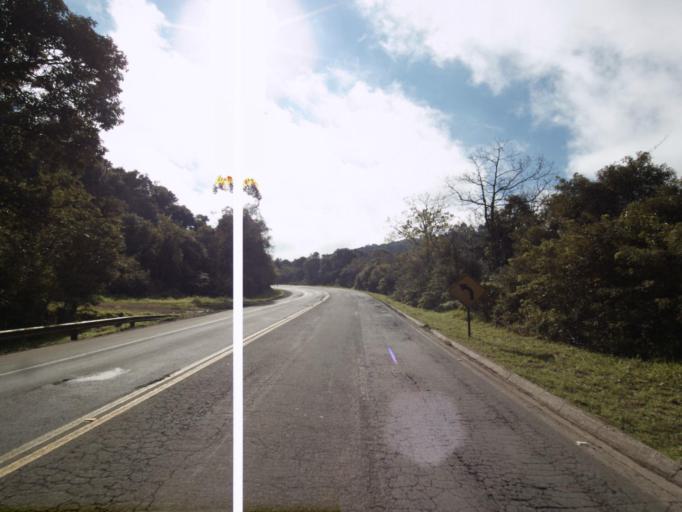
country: BR
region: Rio Grande do Sul
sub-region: Frederico Westphalen
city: Frederico Westphalen
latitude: -27.1368
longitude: -53.2136
